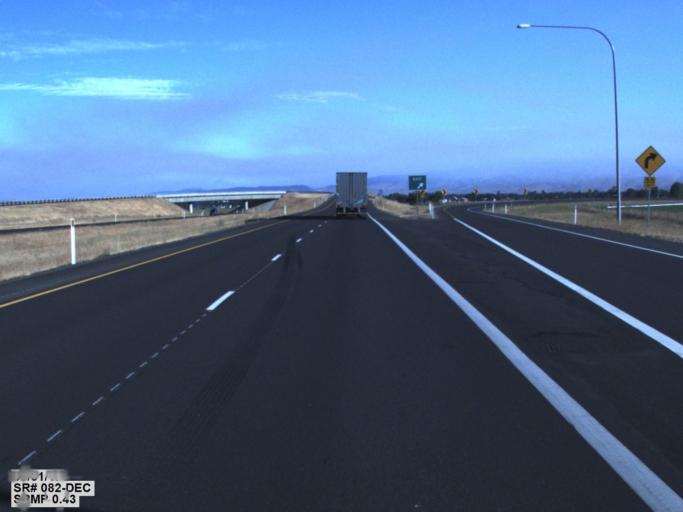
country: US
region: Washington
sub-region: Kittitas County
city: Ellensburg
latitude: 46.9650
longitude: -120.5077
